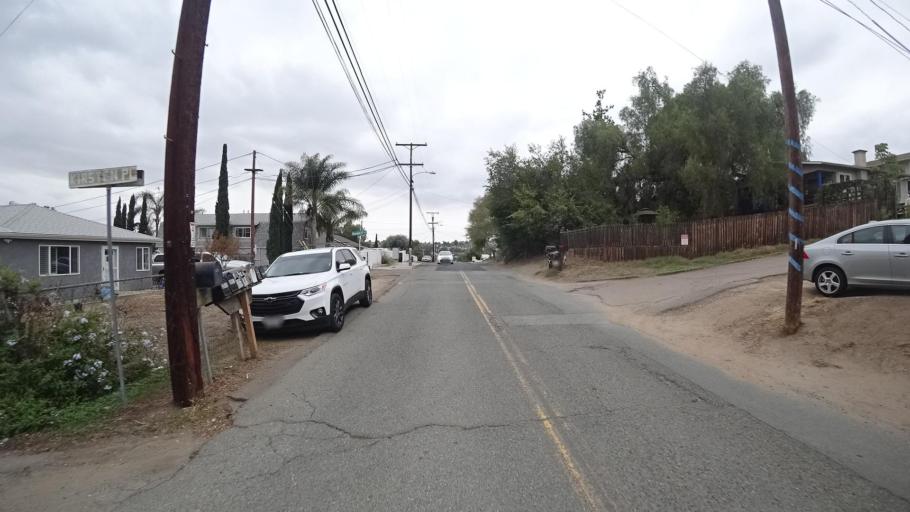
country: US
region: California
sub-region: San Diego County
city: Spring Valley
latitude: 32.7362
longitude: -117.0046
